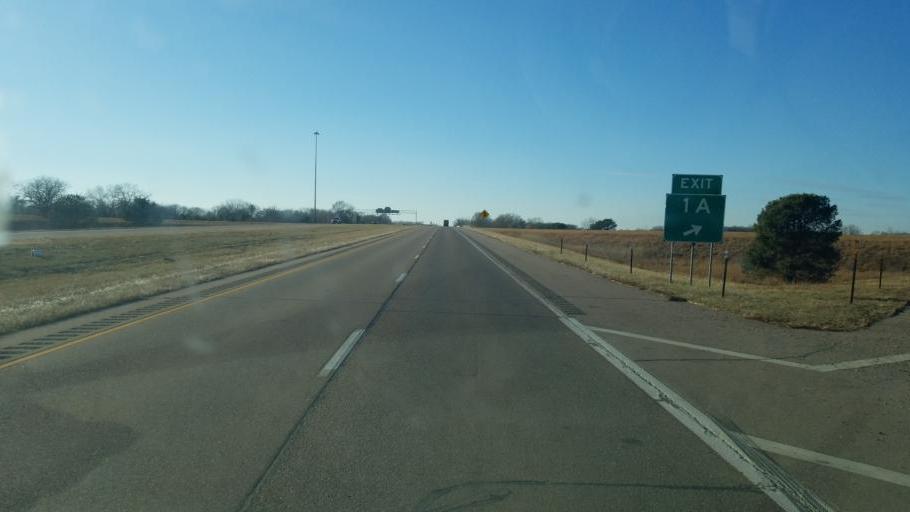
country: US
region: Nebraska
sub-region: Dakota County
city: South Sioux City
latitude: 42.4493
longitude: -96.4369
